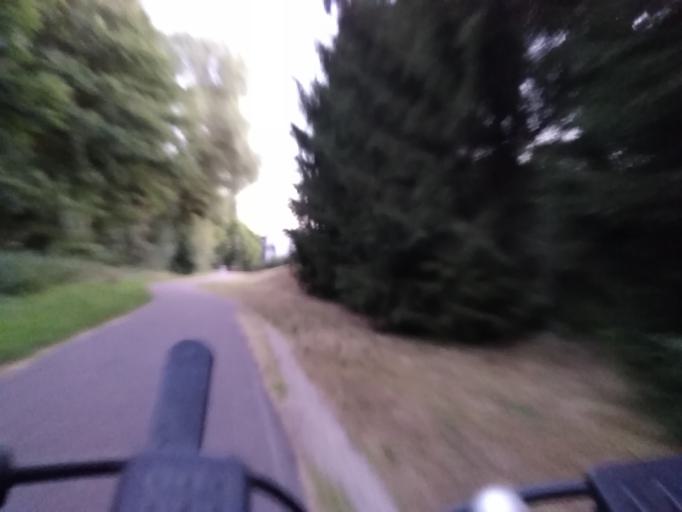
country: FR
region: Lorraine
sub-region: Departement de la Moselle
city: Neufgrange
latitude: 49.0785
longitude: 7.0598
